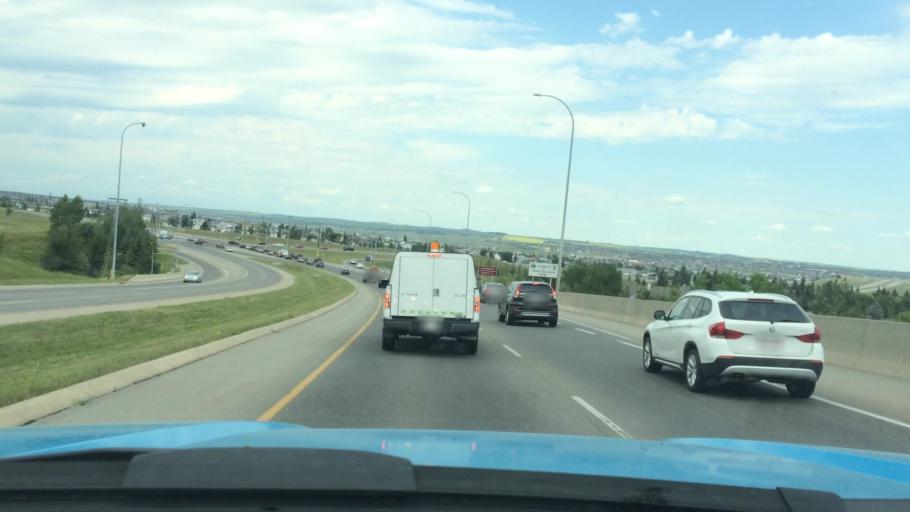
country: CA
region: Alberta
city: Calgary
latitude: 51.1392
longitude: -114.1212
